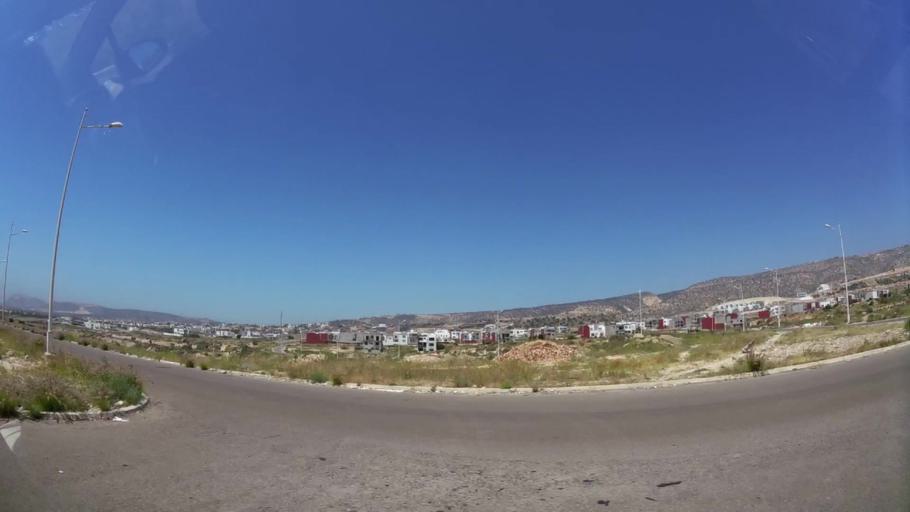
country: MA
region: Oued ed Dahab-Lagouira
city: Dakhla
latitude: 30.4379
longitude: -9.5701
